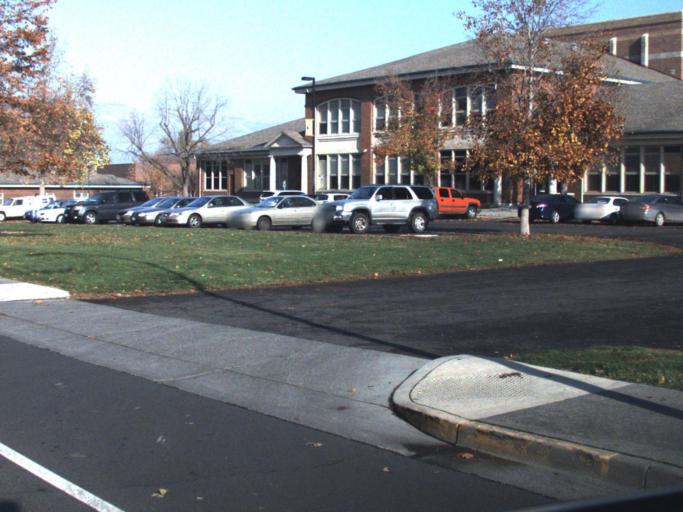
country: US
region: Washington
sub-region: Asotin County
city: Clarkston
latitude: 46.4096
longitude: -117.0456
